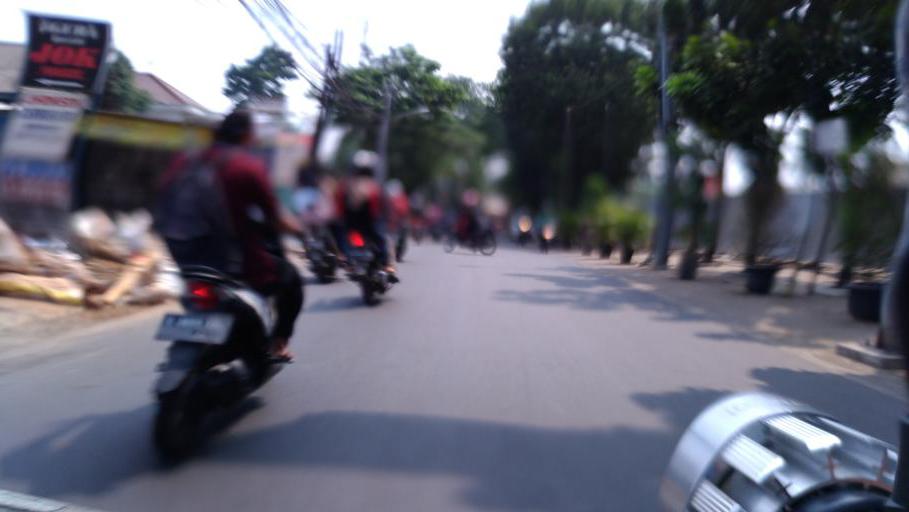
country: ID
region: West Java
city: Depok
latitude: -6.3515
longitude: 106.8794
